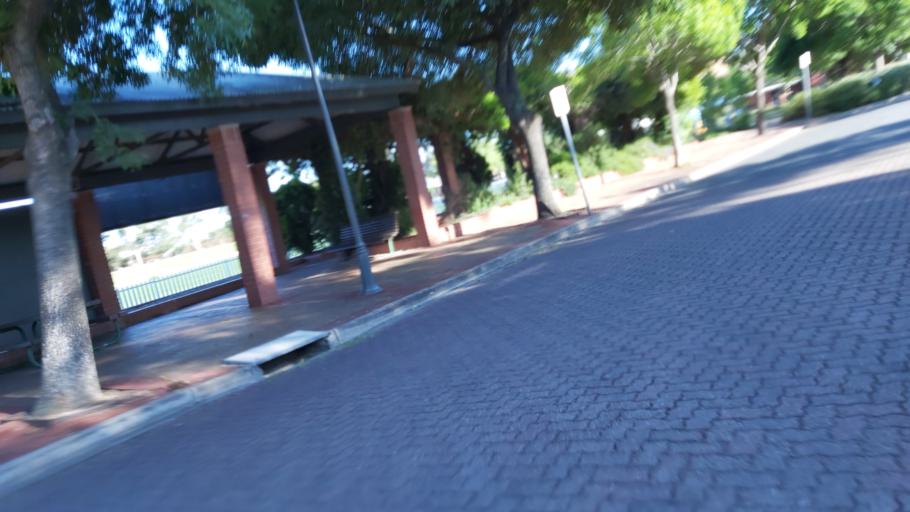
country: AU
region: South Australia
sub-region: Unley
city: Unley
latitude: -34.9502
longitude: 138.6128
